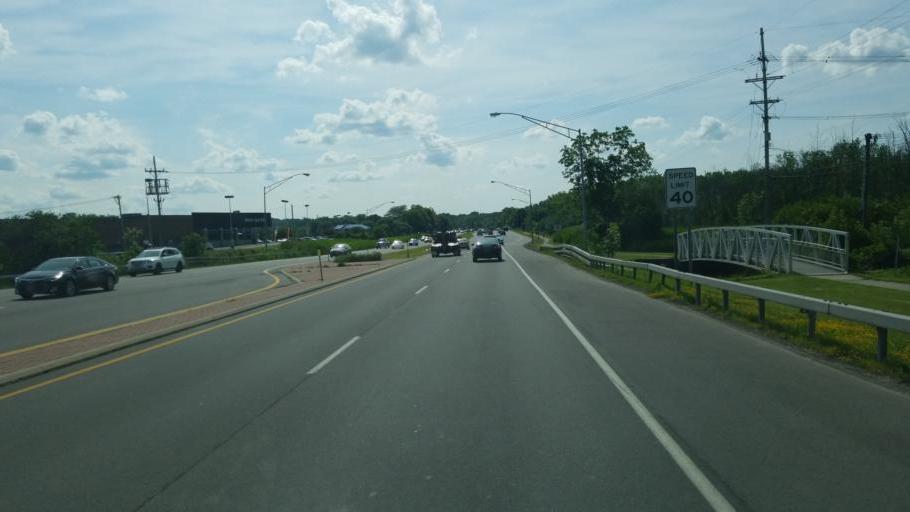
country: US
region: New York
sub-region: Ontario County
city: Canandaigua
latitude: 42.8782
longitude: -77.2690
